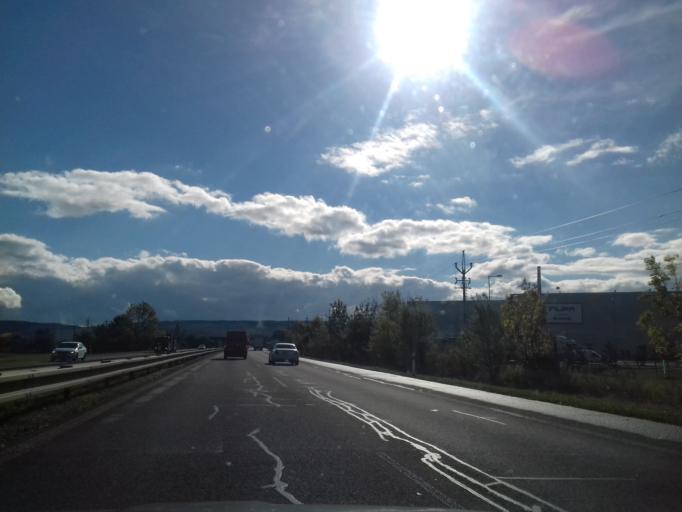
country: CZ
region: Central Bohemia
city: Kosmonosy
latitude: 50.4301
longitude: 14.9436
